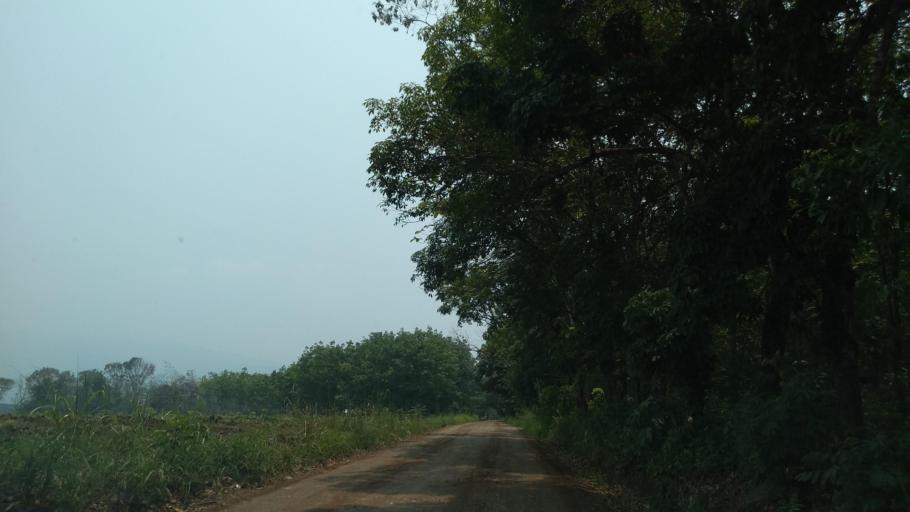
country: MX
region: Veracruz
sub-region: Tezonapa
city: Laguna Chica (Pueblo Nuevo)
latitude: 18.5097
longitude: -96.7687
